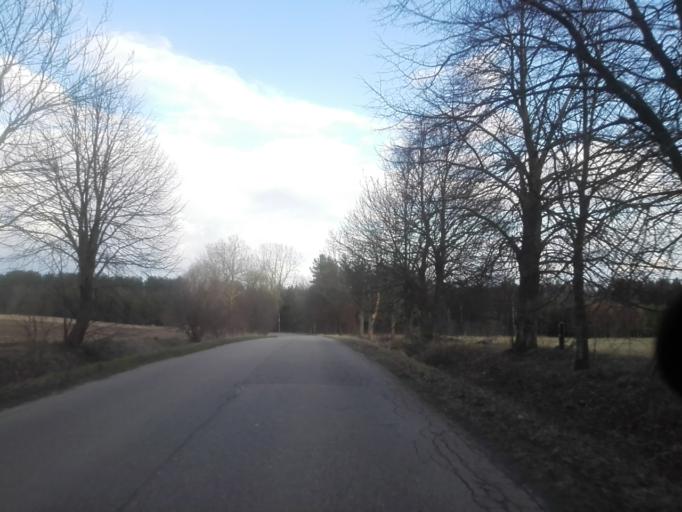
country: PL
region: Podlasie
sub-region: Suwalki
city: Suwalki
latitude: 54.2176
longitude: 22.8543
